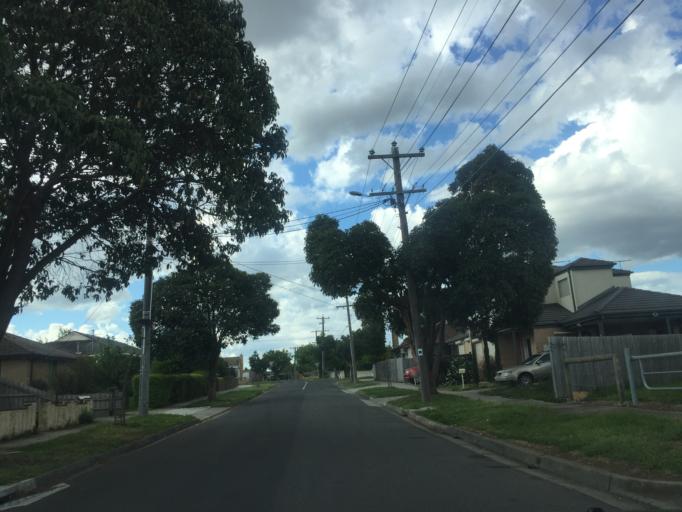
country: AU
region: Victoria
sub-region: Darebin
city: Reservoir
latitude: -37.7058
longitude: 145.0121
